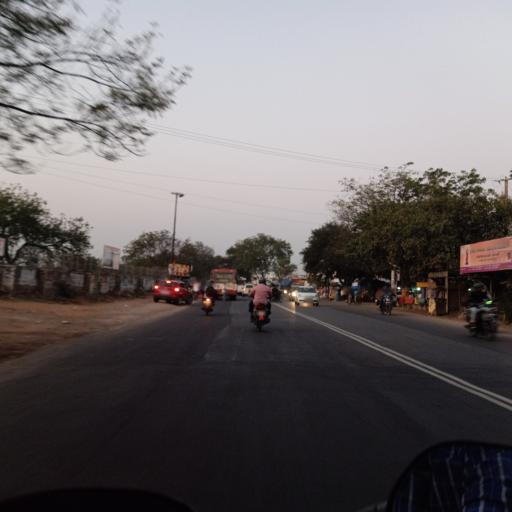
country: IN
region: Telangana
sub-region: Rangareddi
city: Secunderabad
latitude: 17.5468
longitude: 78.5349
